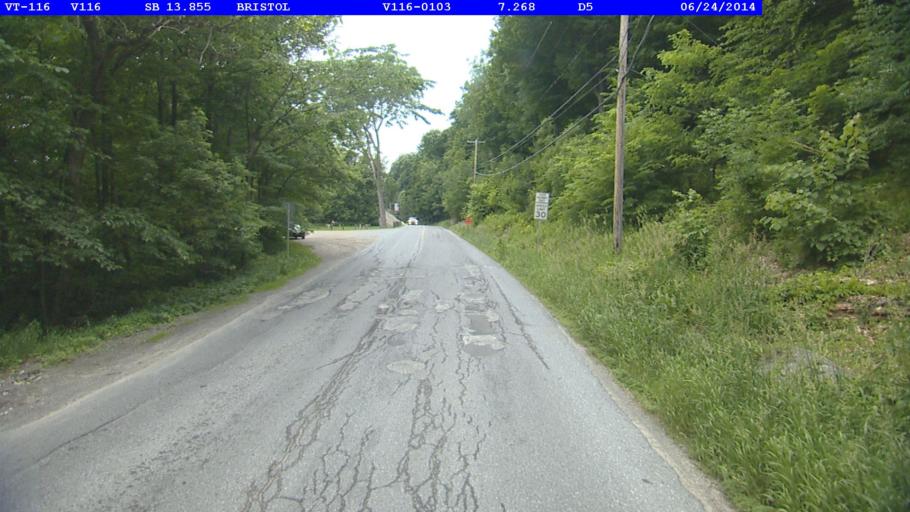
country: US
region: Vermont
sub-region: Addison County
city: Bristol
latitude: 44.1292
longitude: -73.0674
